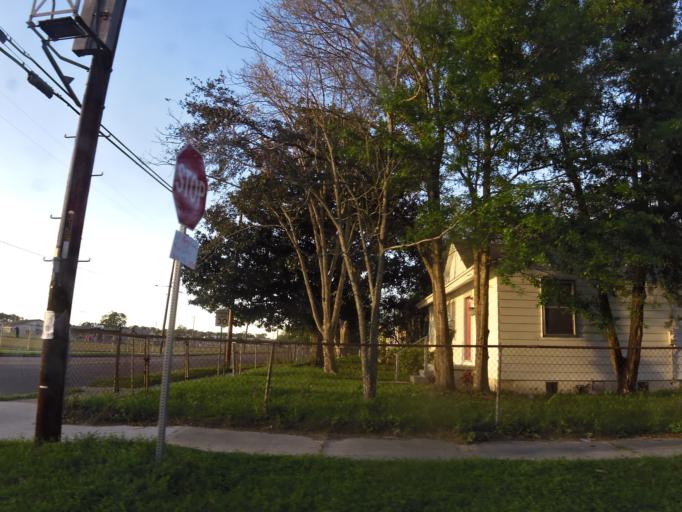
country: US
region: Florida
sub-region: Duval County
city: Jacksonville
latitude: 30.3403
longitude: -81.7226
